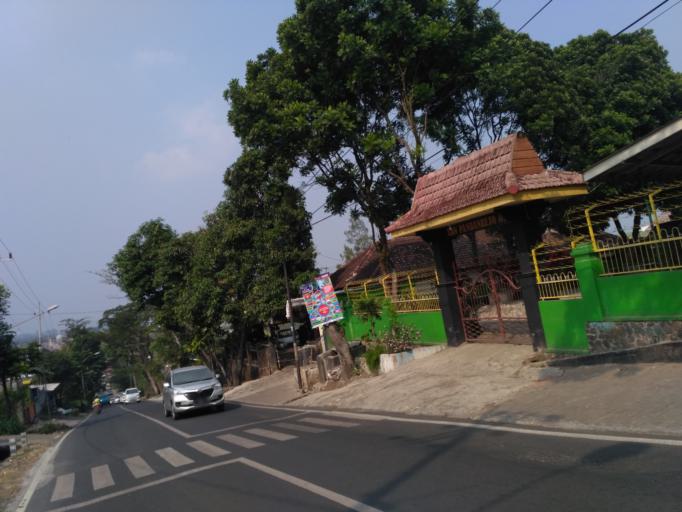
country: ID
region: East Java
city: Batu
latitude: -7.8646
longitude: 112.5454
